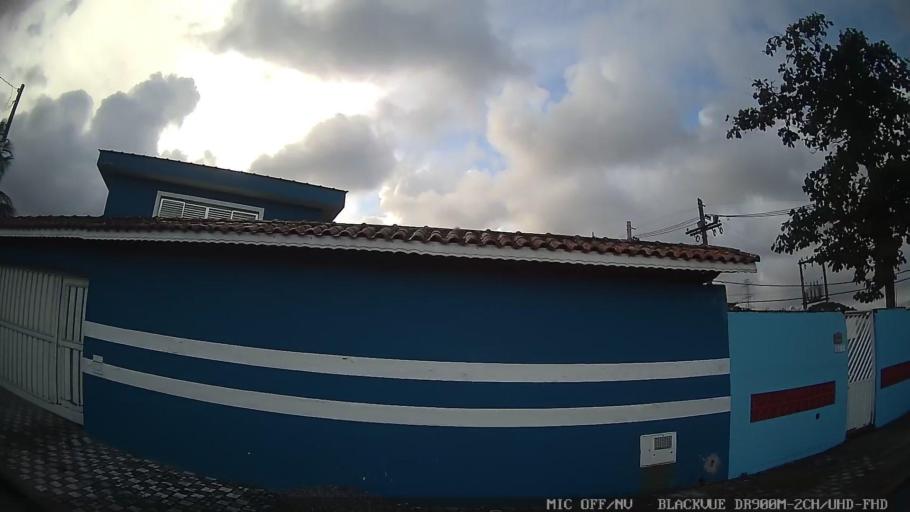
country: BR
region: Sao Paulo
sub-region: Mongagua
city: Mongagua
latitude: -24.1164
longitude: -46.6731
